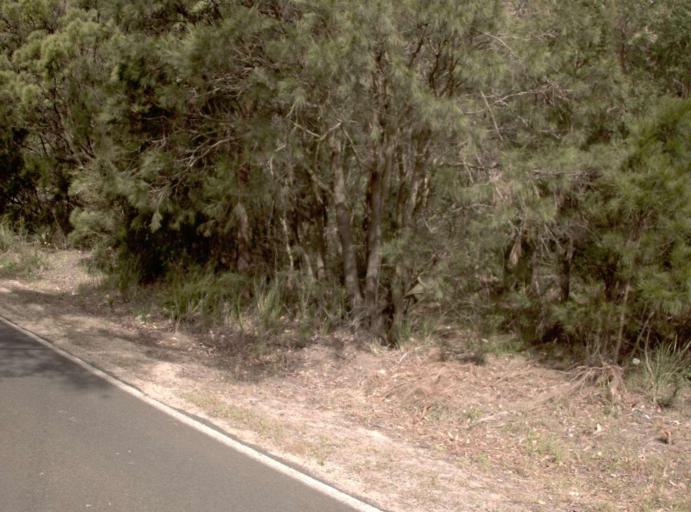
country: AU
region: Victoria
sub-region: Latrobe
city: Traralgon
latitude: -38.3811
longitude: 146.7677
